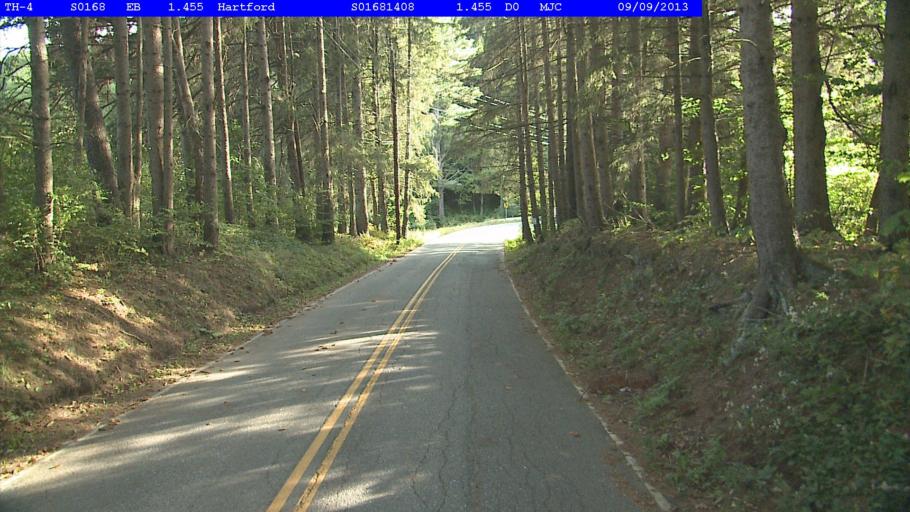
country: US
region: Vermont
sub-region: Windsor County
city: White River Junction
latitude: 43.6424
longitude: -72.4004
